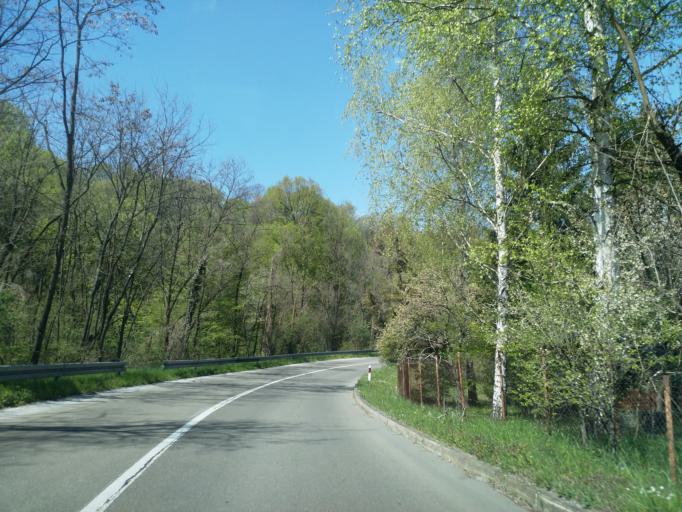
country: RS
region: Central Serbia
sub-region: Belgrade
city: Lazarevac
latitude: 44.3560
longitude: 20.3523
